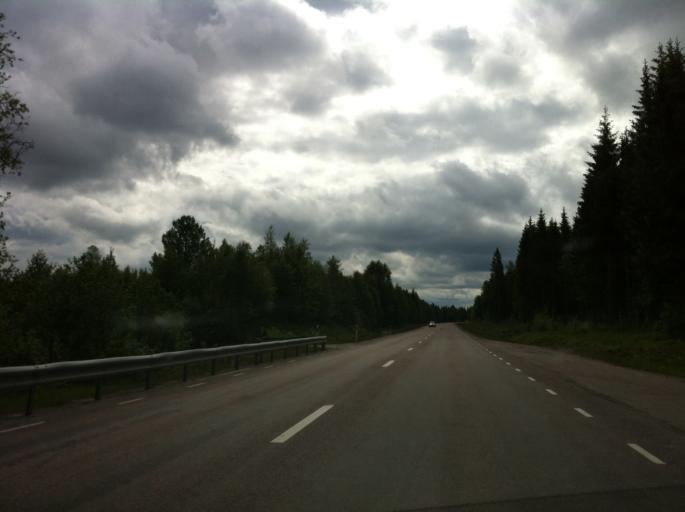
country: SE
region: Vaermland
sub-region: Sunne Kommun
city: Sunne
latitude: 59.7678
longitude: 13.1035
